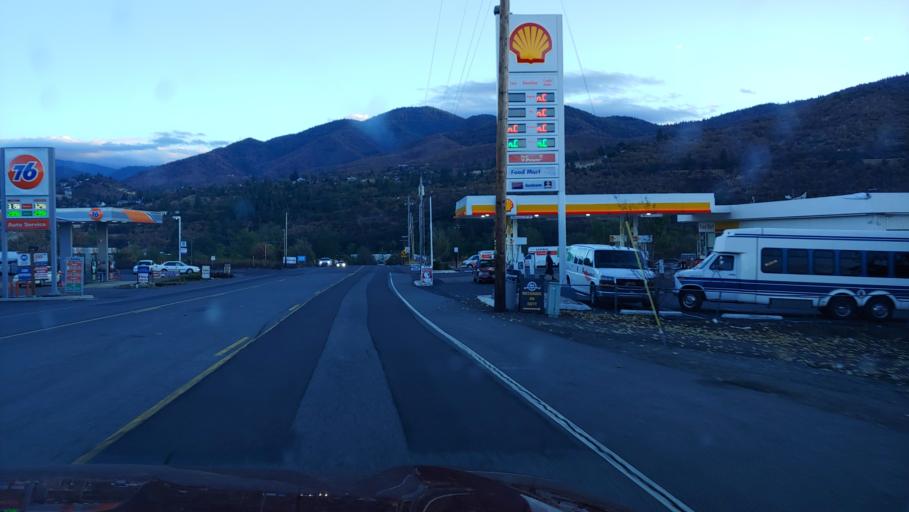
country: US
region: Oregon
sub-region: Jackson County
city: Ashland
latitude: 42.2260
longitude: -122.7406
